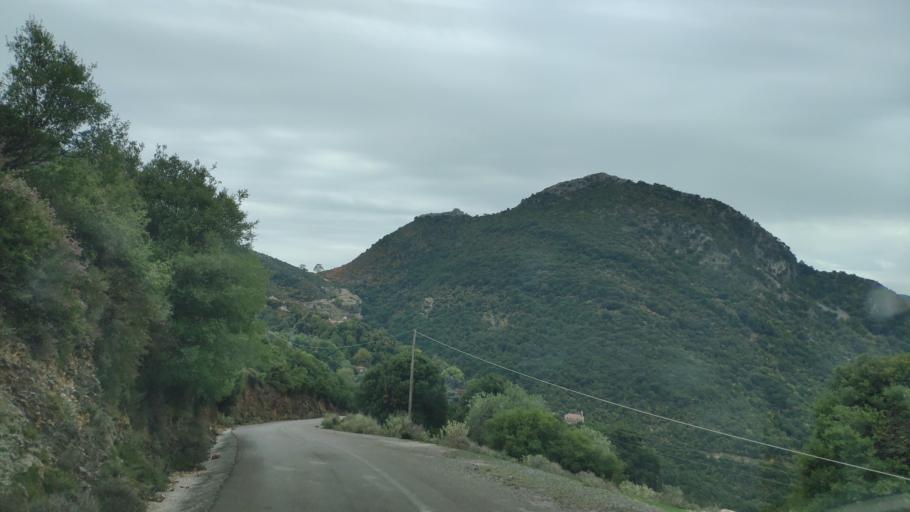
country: GR
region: Epirus
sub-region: Nomos Prevezis
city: Kanalaki
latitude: 39.3487
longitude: 20.6487
